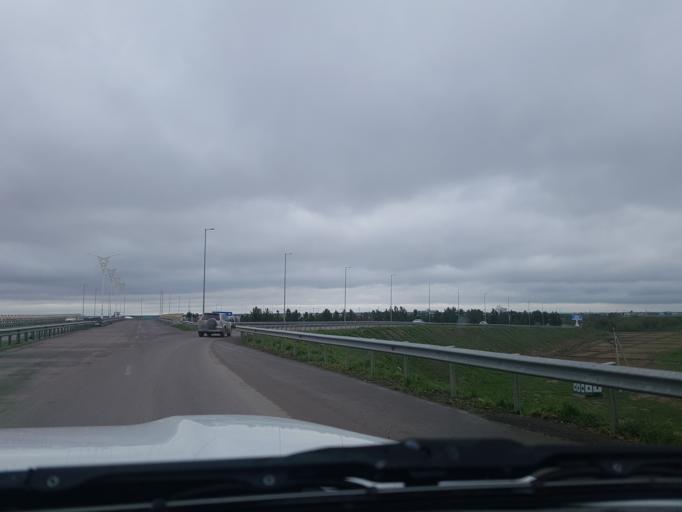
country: TM
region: Mary
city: Mary
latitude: 37.5975
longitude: 61.8873
